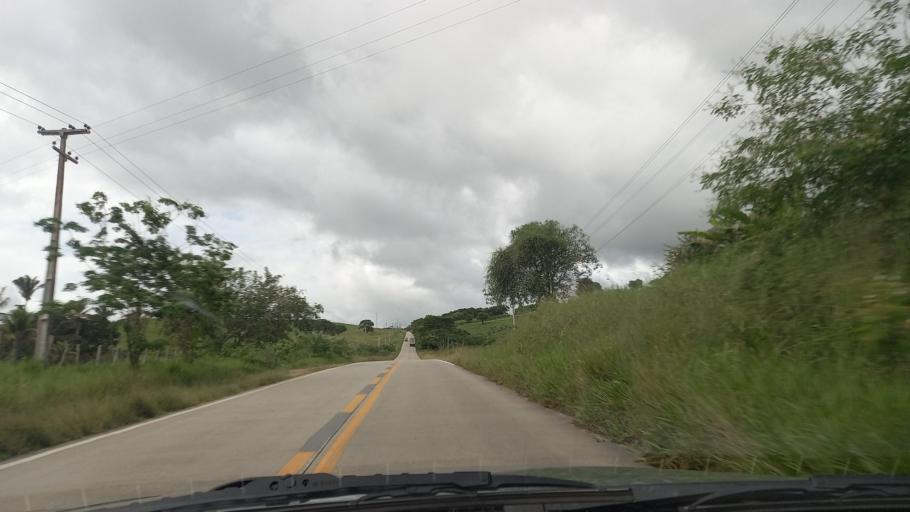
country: BR
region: Pernambuco
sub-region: Quipapa
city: Quipapa
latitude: -8.8029
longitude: -36.0036
